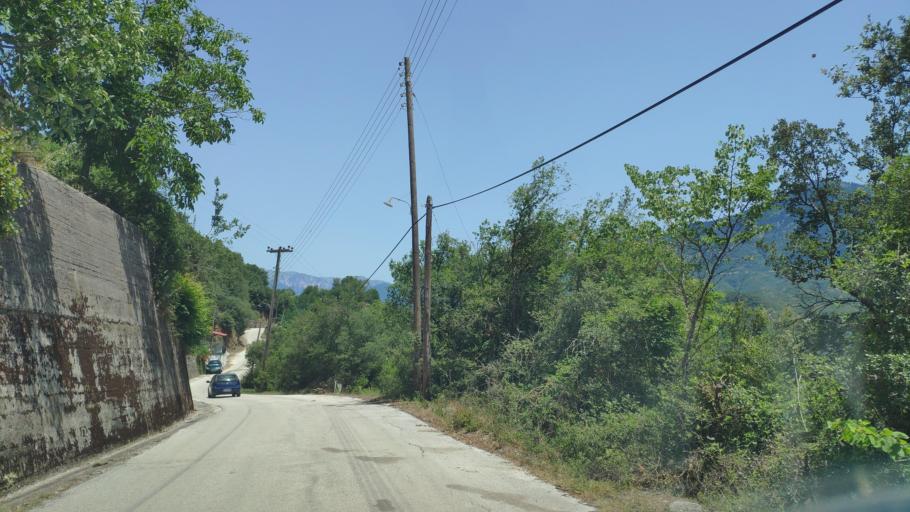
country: GR
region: Epirus
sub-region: Nomos Artas
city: Ano Kalentini
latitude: 39.2054
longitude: 21.3424
